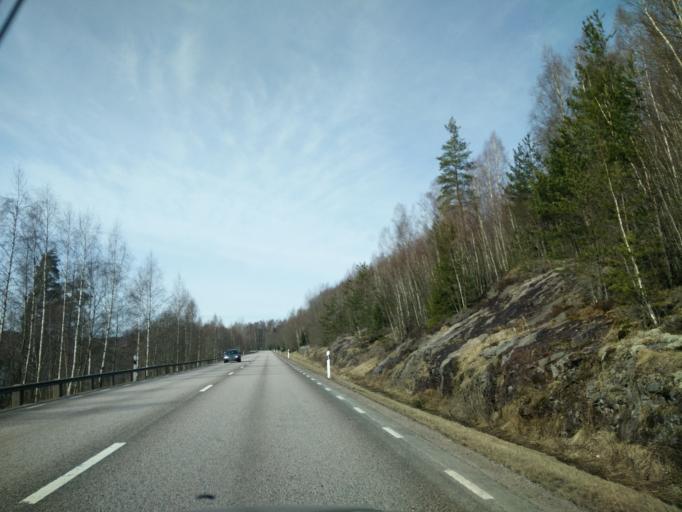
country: SE
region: Vaermland
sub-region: Hagfors Kommun
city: Hagfors
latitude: 60.0321
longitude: 13.6059
